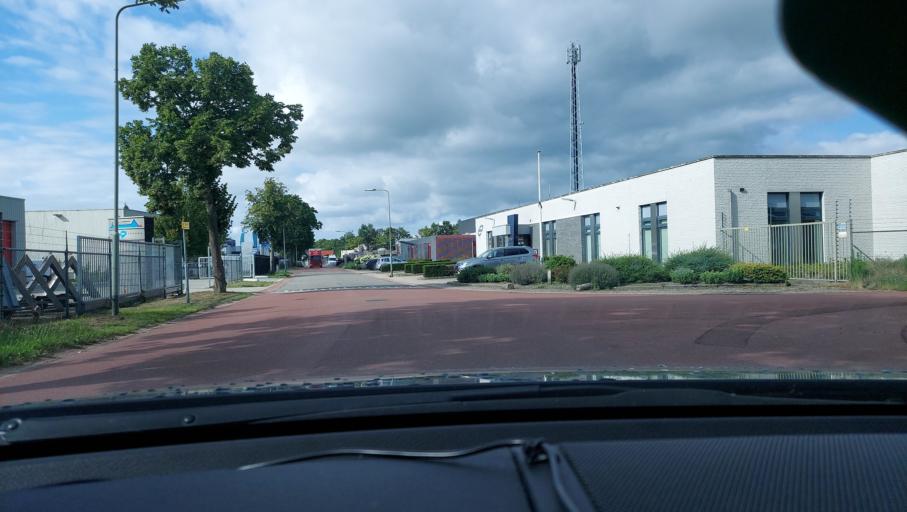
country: NL
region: Limburg
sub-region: Gemeente Beesel
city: Offenbeek
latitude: 51.2906
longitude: 6.0904
